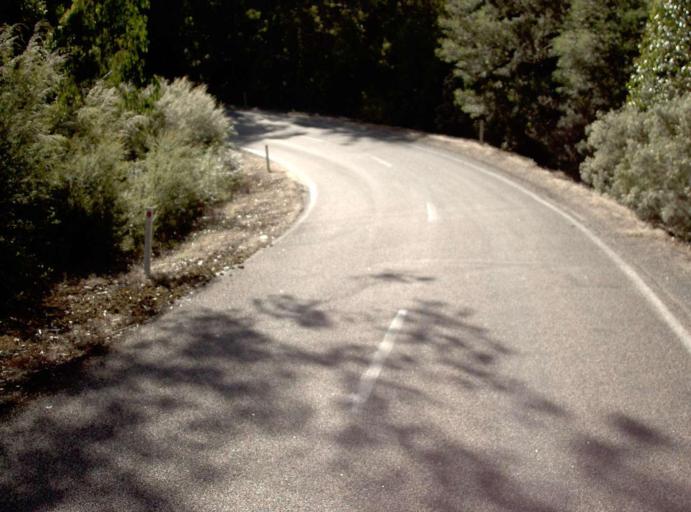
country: AU
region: Victoria
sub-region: East Gippsland
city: Lakes Entrance
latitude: -37.5426
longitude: 148.5424
